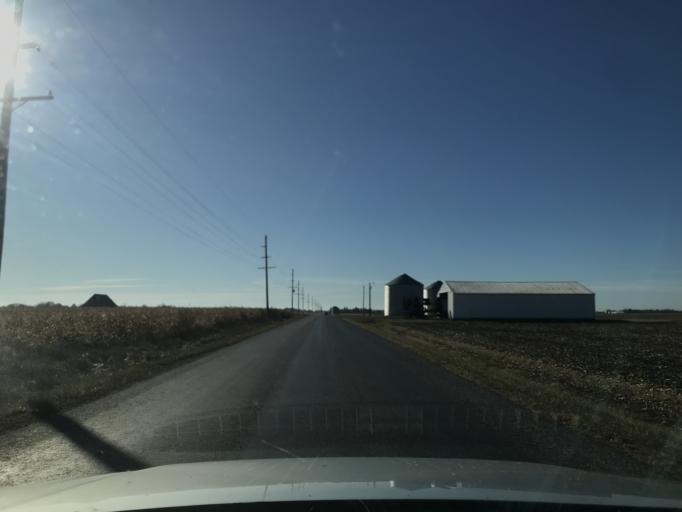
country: US
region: Illinois
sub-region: Hancock County
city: Carthage
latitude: 40.4788
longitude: -91.1781
